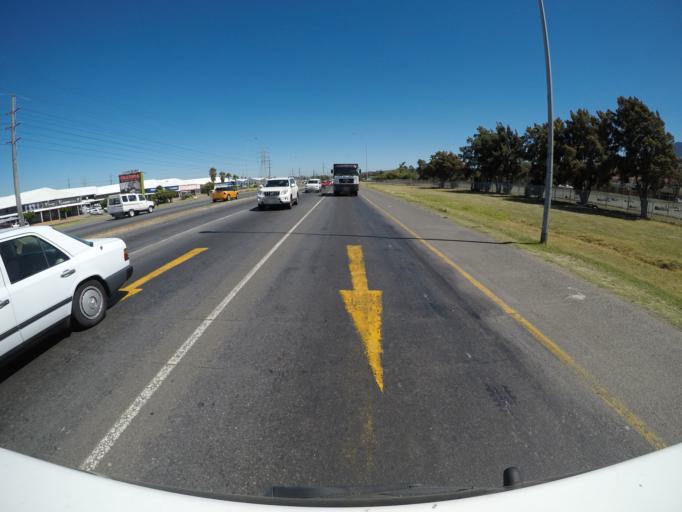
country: ZA
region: Western Cape
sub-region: Cape Winelands District Municipality
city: Stellenbosch
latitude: -34.0943
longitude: 18.8449
